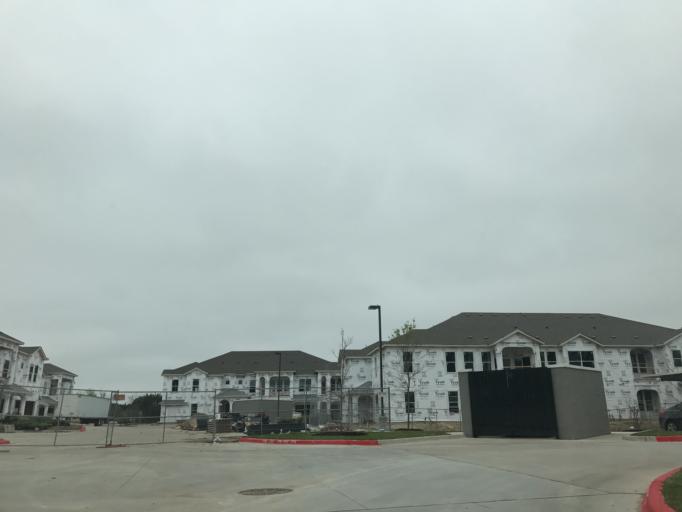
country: US
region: Texas
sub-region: Travis County
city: Wells Branch
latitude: 30.4674
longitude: -97.6868
